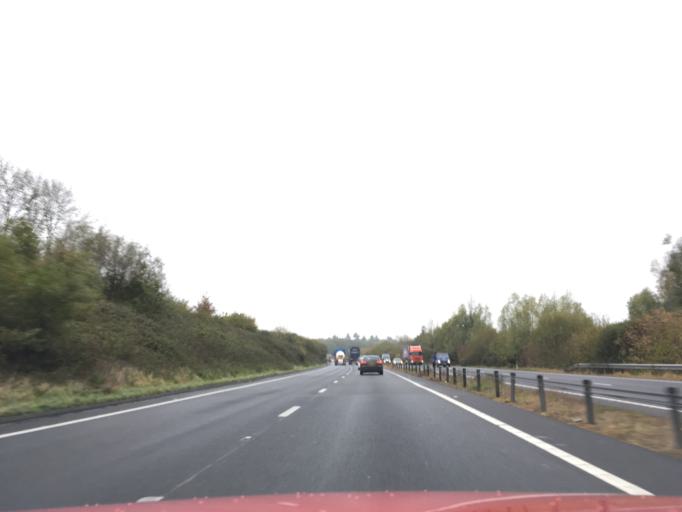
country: GB
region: England
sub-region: West Berkshire
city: Newbury
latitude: 51.3850
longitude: -1.3623
